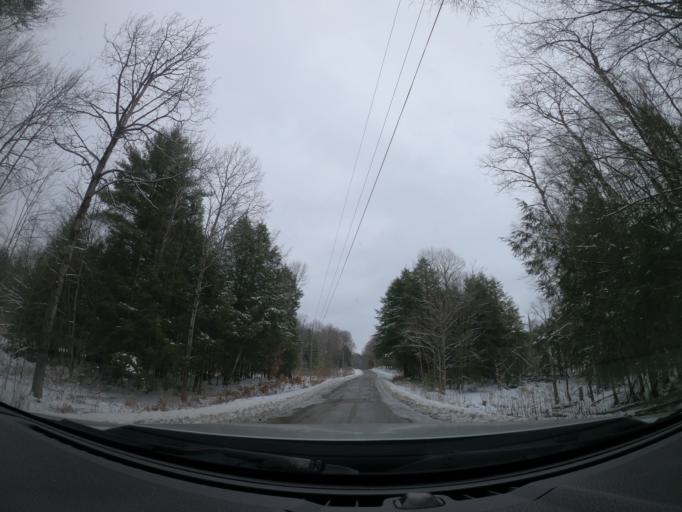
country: US
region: New York
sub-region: Cayuga County
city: Moravia
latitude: 42.7331
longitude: -76.2896
